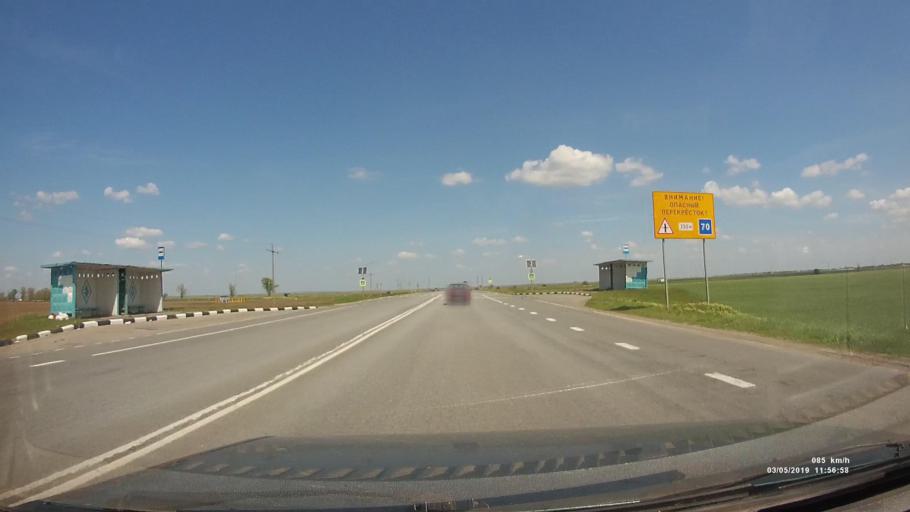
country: RU
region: Rostov
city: Bagayevskaya
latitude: 47.2009
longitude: 40.3065
